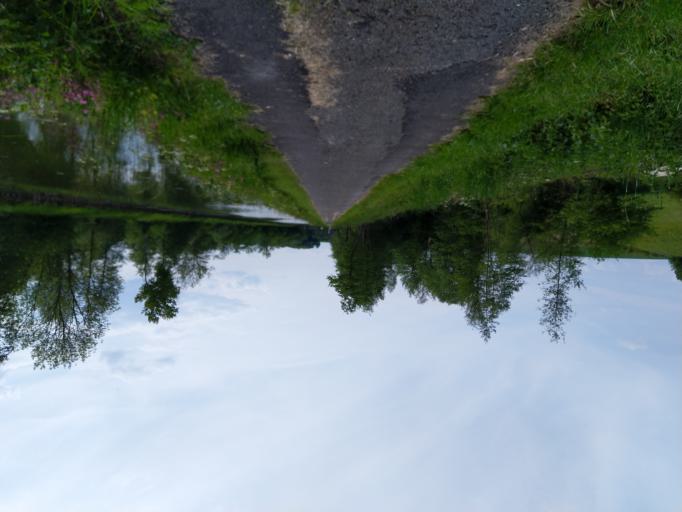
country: FR
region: Picardie
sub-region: Departement de l'Aisne
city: Etreux
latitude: 49.9642
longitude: 3.6184
